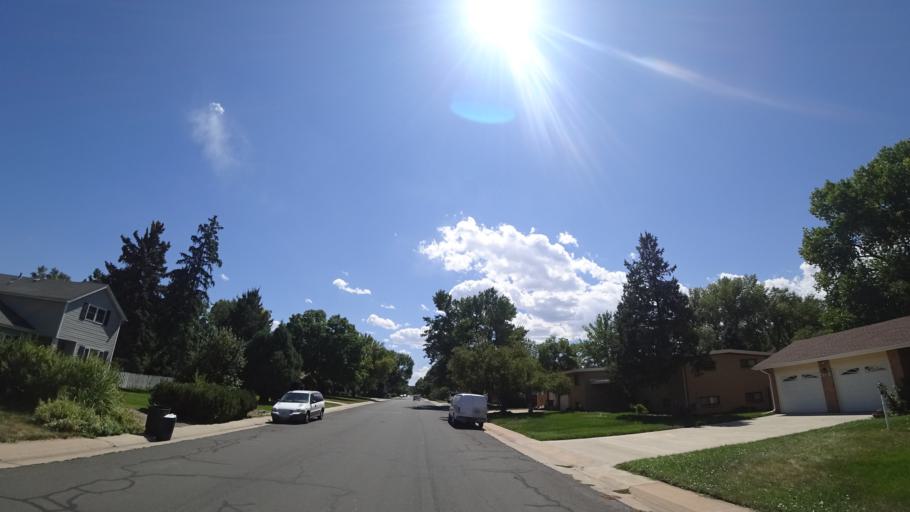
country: US
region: Colorado
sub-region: Arapahoe County
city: Greenwood Village
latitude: 39.6088
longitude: -104.9810
